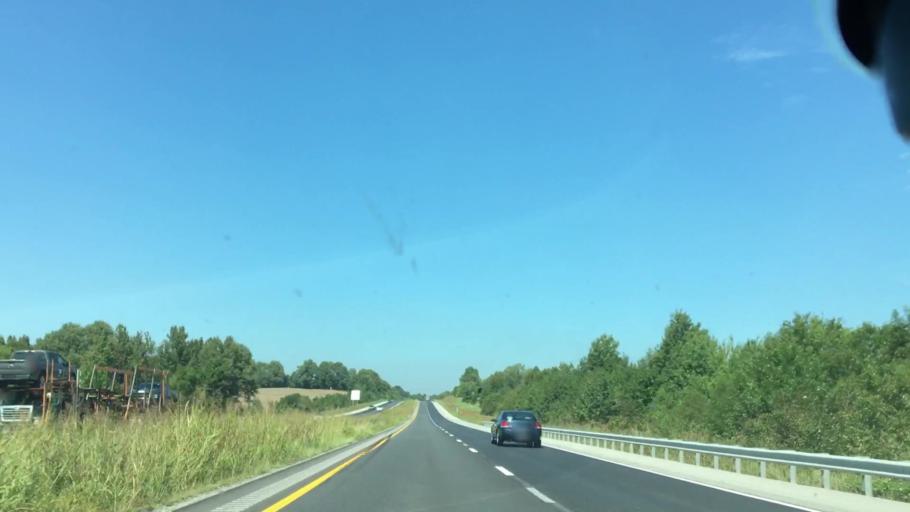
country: US
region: Kentucky
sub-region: Hopkins County
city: Madisonville
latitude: 37.4461
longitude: -87.4761
